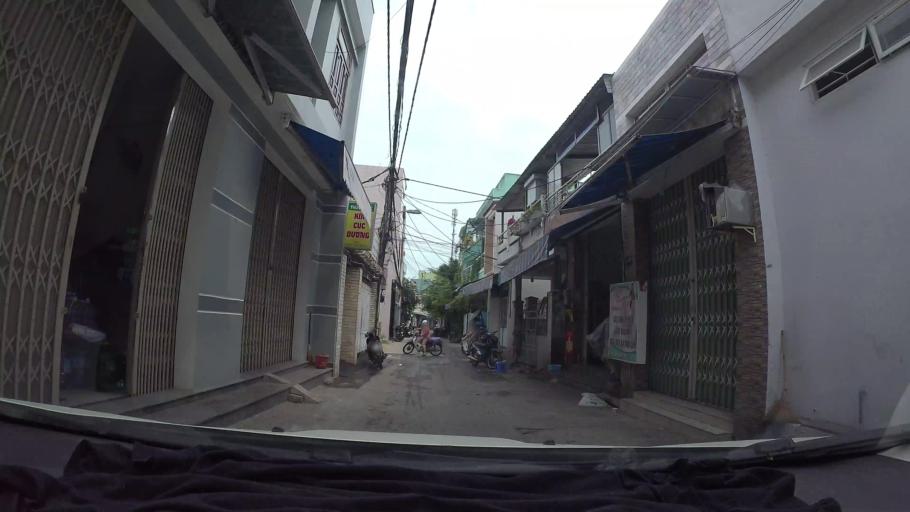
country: VN
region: Da Nang
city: Da Nang
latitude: 16.0835
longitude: 108.2165
